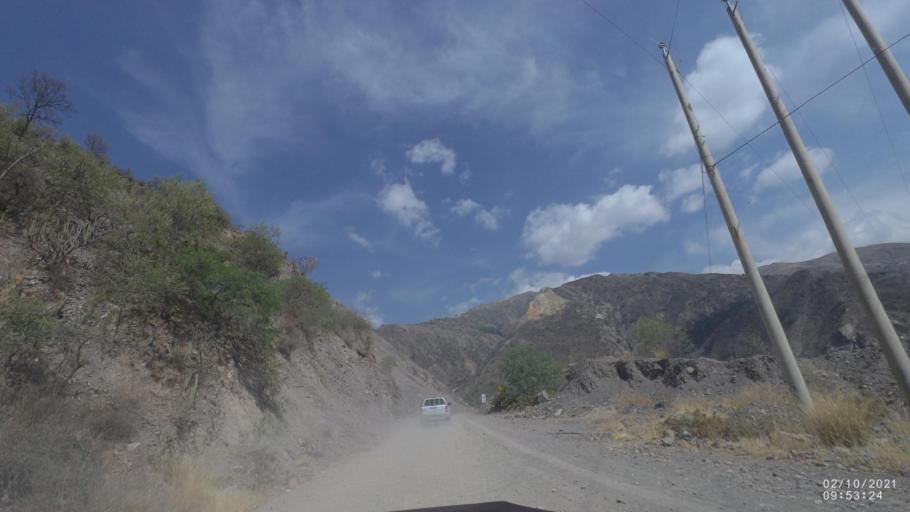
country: BO
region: Cochabamba
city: Irpa Irpa
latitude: -17.8014
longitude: -66.3488
